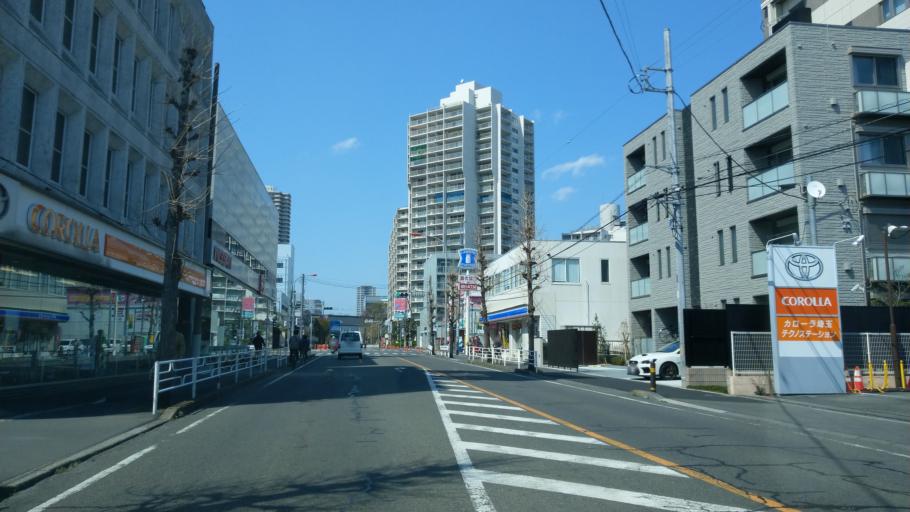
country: JP
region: Saitama
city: Yono
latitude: 35.8879
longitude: 139.6301
